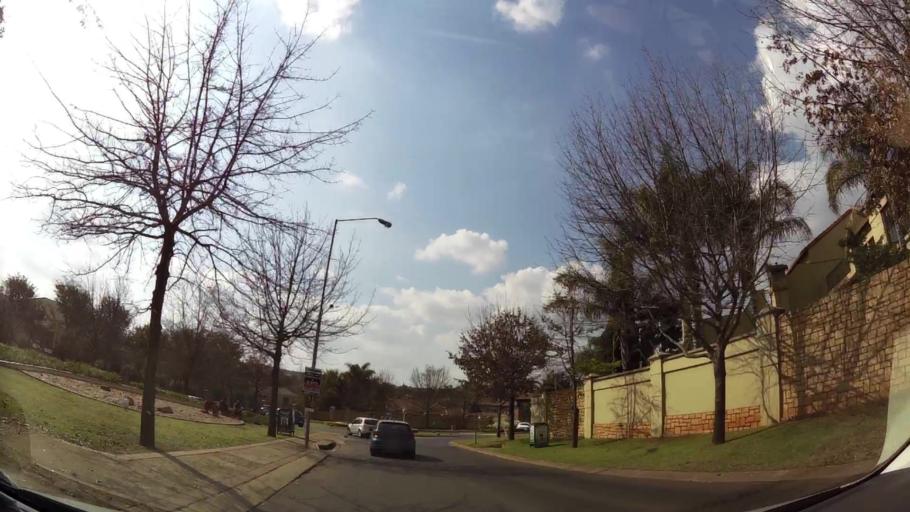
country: ZA
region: Gauteng
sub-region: City of Tshwane Metropolitan Municipality
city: Pretoria
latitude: -25.7994
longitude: 28.3269
